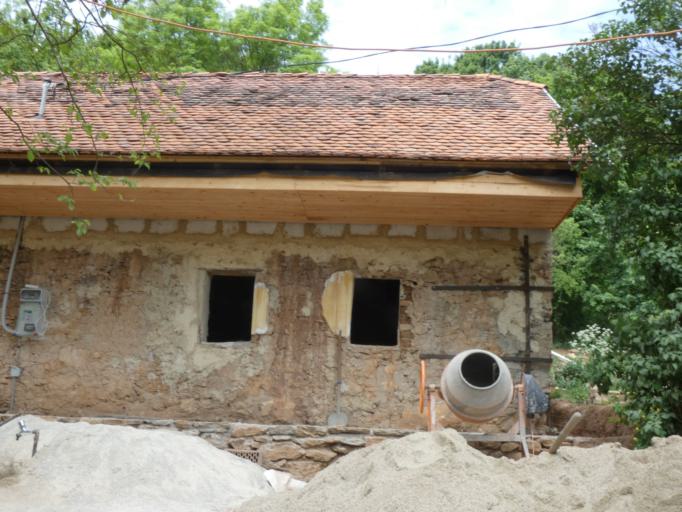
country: HU
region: Borsod-Abauj-Zemplen
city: Rudabanya
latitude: 48.4856
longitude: 20.5484
